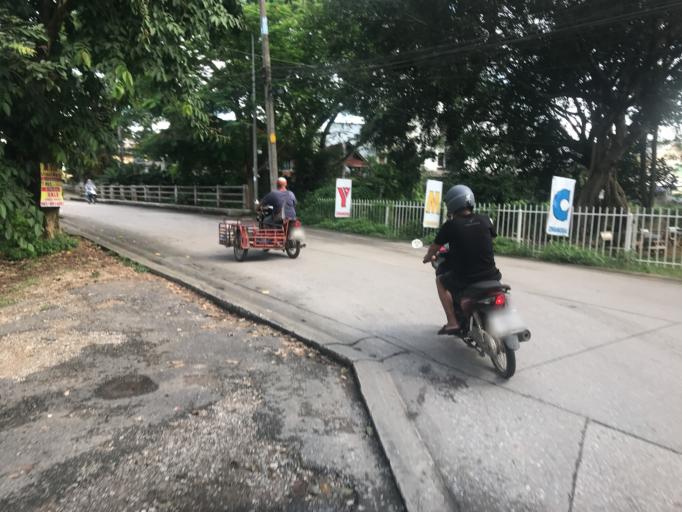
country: TH
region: Chiang Rai
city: Chiang Rai
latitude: 19.9134
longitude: 99.8312
